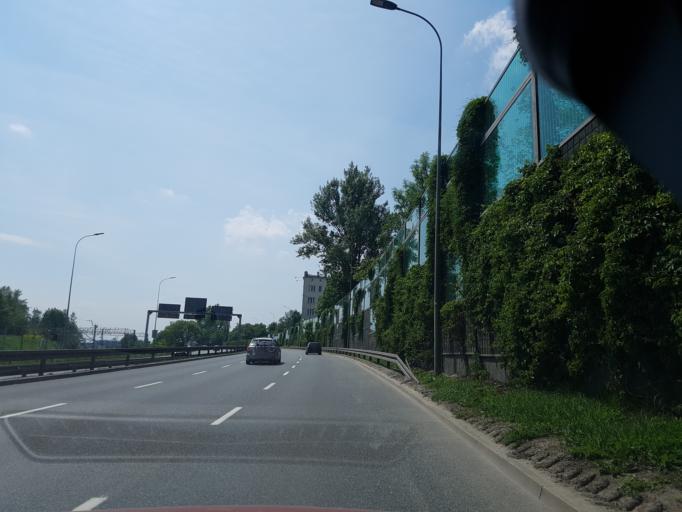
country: PL
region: Lesser Poland Voivodeship
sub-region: Krakow
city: Krakow
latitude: 50.0409
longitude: 19.9563
